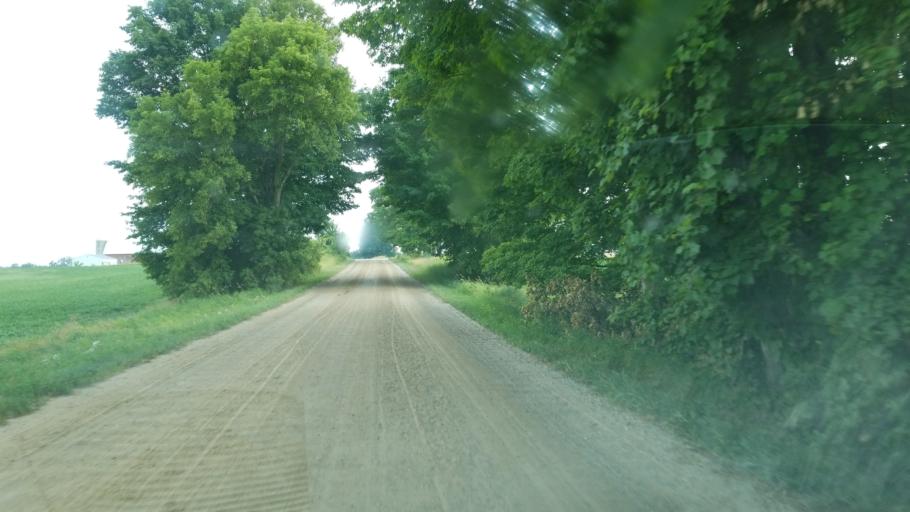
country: US
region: Michigan
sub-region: Mecosta County
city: Canadian Lakes
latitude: 43.5441
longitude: -85.3632
